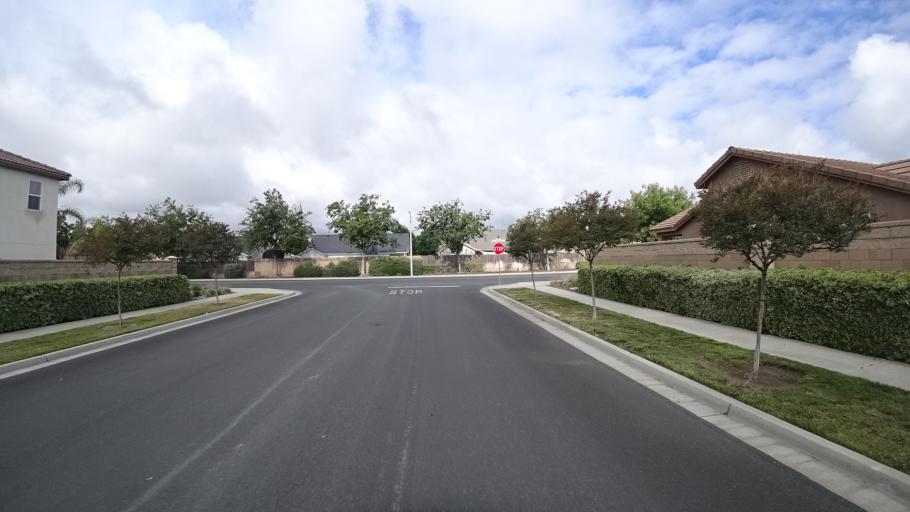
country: US
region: California
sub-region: Kings County
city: Lucerne
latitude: 36.3536
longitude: -119.6681
